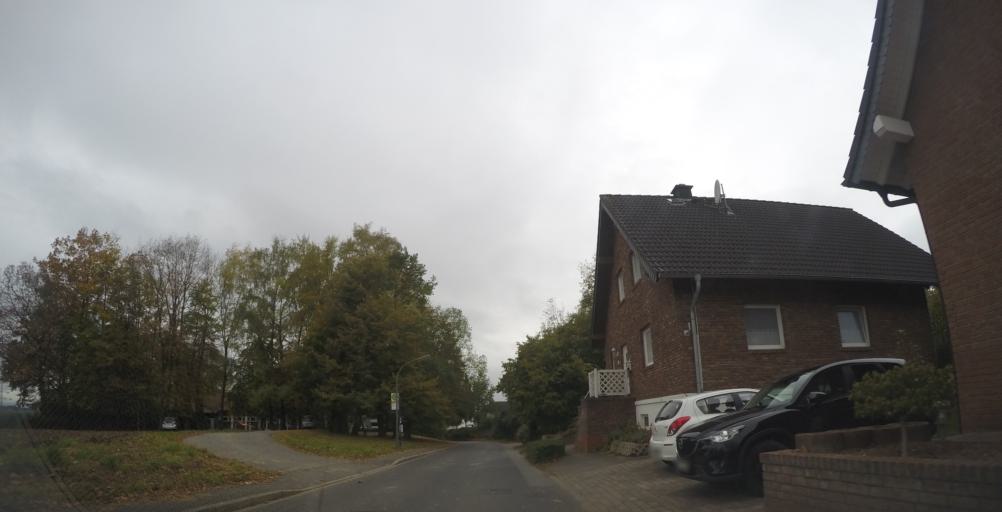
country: DE
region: North Rhine-Westphalia
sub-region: Regierungsbezirk Arnsberg
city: Unna
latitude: 51.4817
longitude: 7.6970
